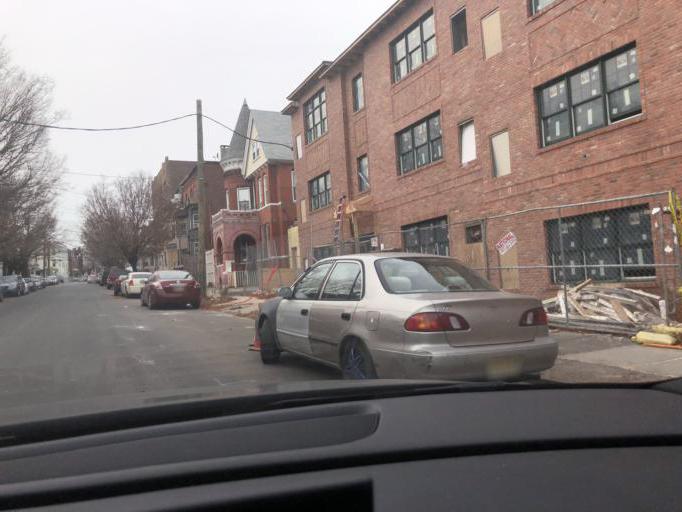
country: US
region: New Jersey
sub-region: Hudson County
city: East Newark
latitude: 40.7570
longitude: -74.1707
